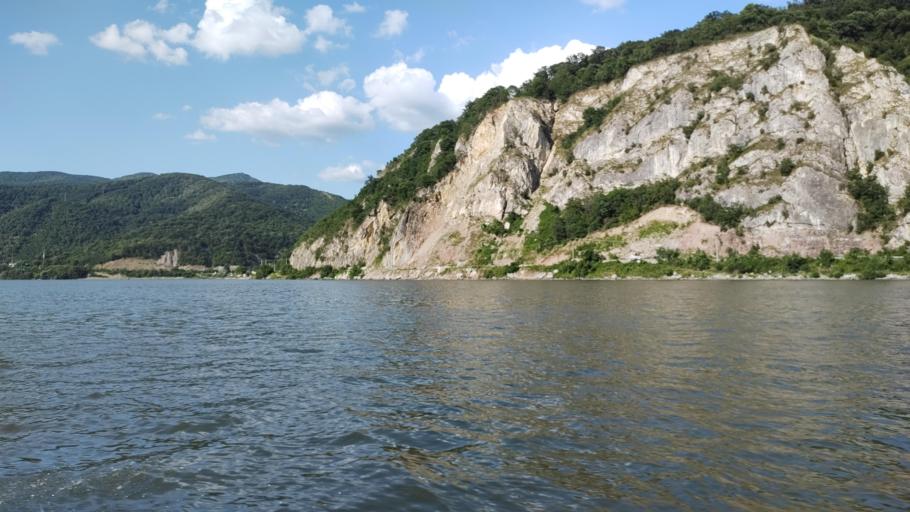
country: RO
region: Caras-Severin
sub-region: Comuna Berzasca
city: Berzasca
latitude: 44.6122
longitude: 22.0035
